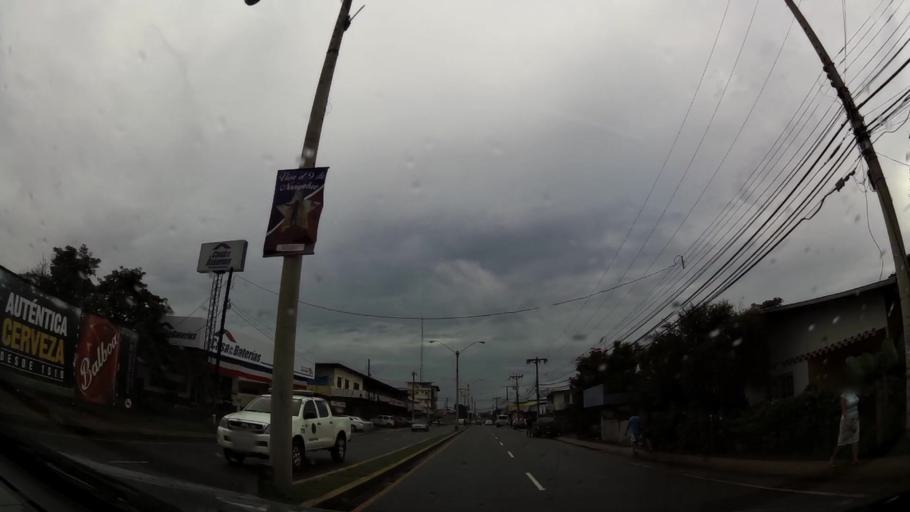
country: PA
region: Veraguas
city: Santiago de Veraguas
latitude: 8.1023
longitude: -80.9747
